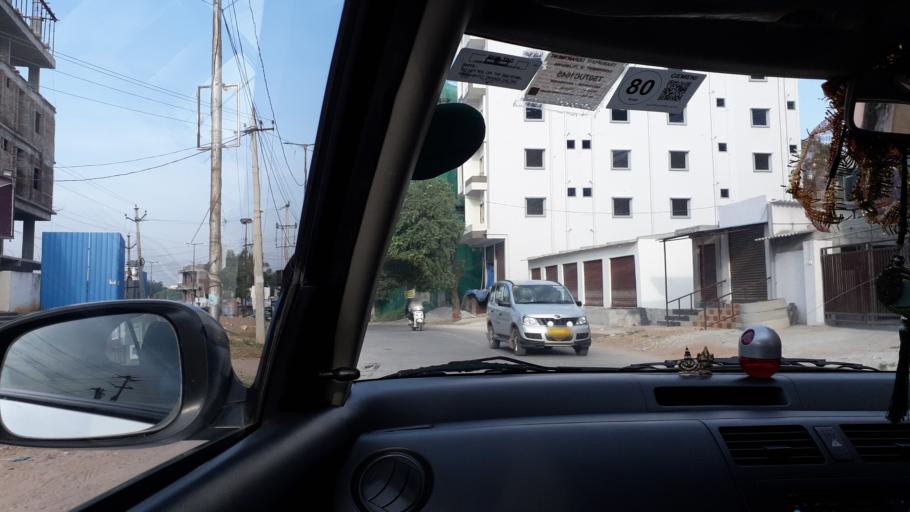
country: IN
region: Telangana
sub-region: Hyderabad
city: Hyderabad
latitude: 17.3947
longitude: 78.3847
